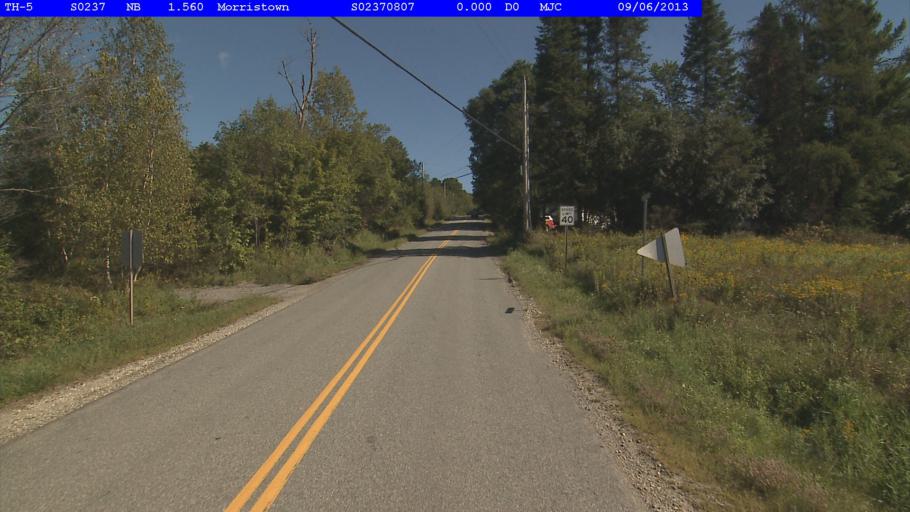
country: US
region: Vermont
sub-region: Lamoille County
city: Morristown
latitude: 44.5026
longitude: -72.6546
